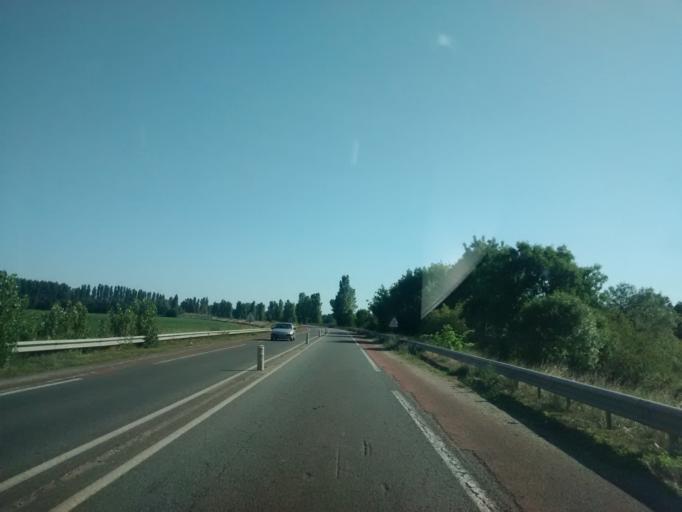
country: FR
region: Aquitaine
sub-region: Departement de la Gironde
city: Libourne
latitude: 44.8869
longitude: -0.2196
